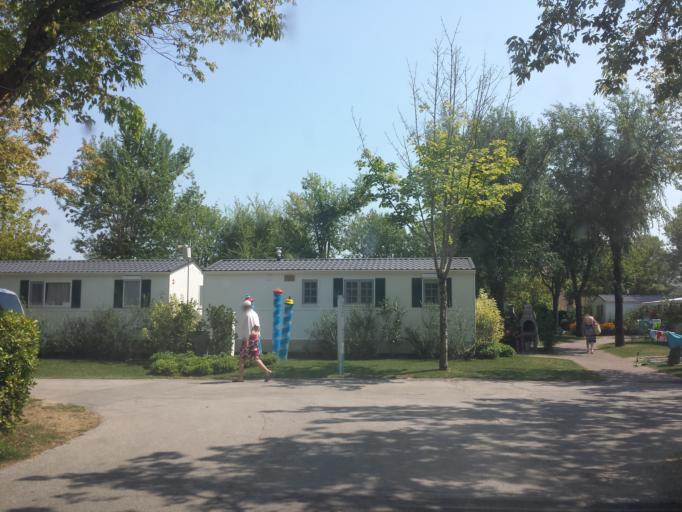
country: IT
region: Veneto
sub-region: Provincia di Venezia
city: Cavallino
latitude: 45.4771
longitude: 12.5658
